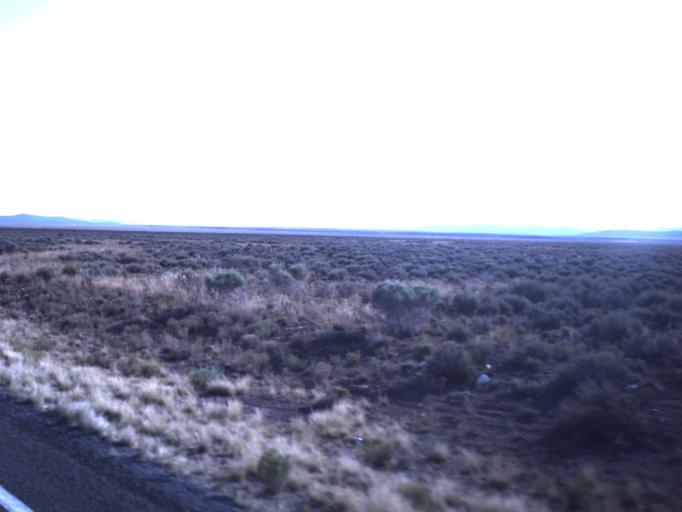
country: US
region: Utah
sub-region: Iron County
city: Enoch
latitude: 37.9170
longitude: -113.0315
